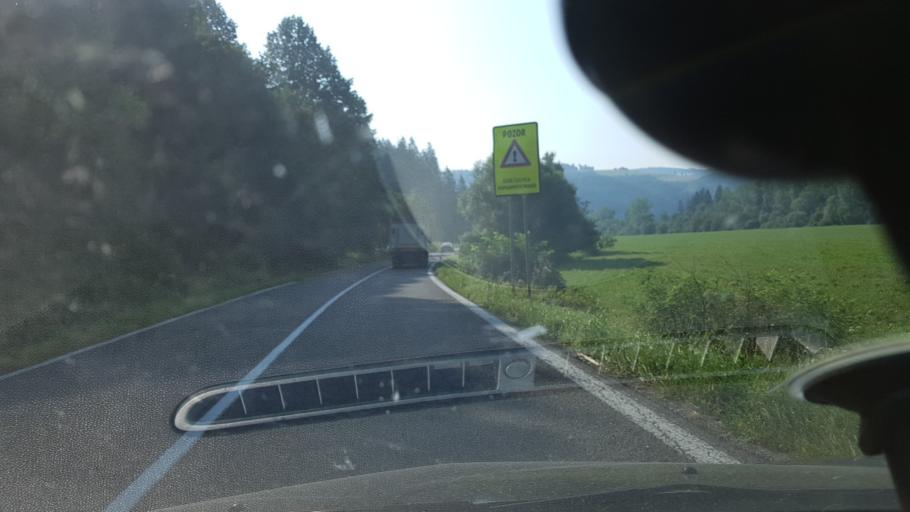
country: SK
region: Zilinsky
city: Tvrdosin
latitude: 49.3010
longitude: 19.4827
